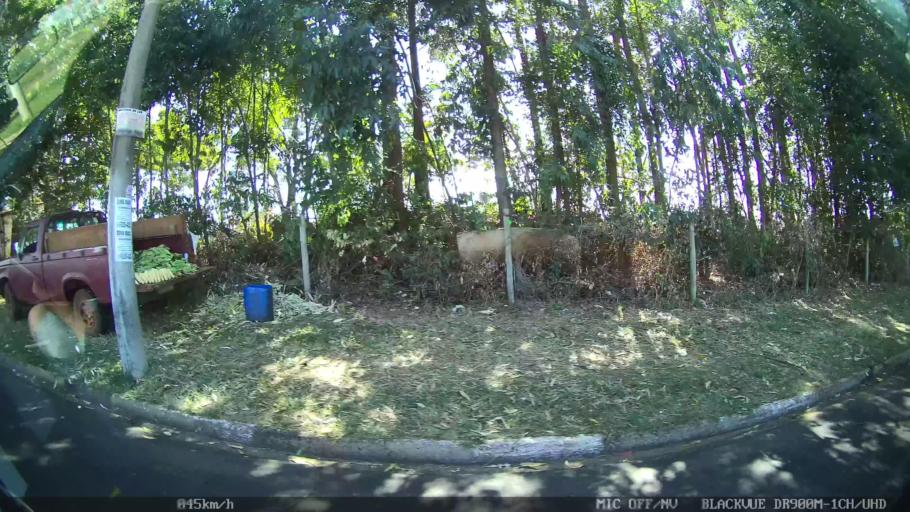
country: BR
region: Sao Paulo
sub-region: Franca
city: Franca
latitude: -20.5488
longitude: -47.4407
